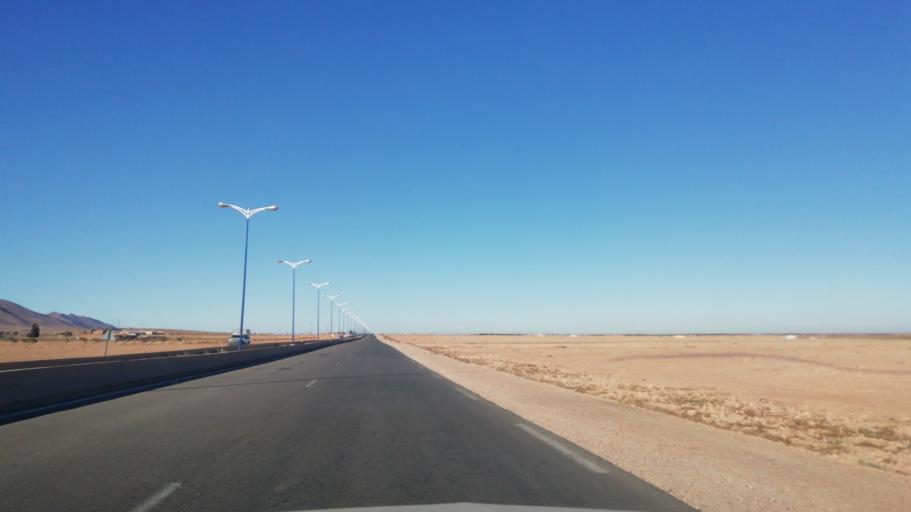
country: DZ
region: Wilaya de Naama
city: Naama
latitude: 33.5719
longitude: -0.2405
